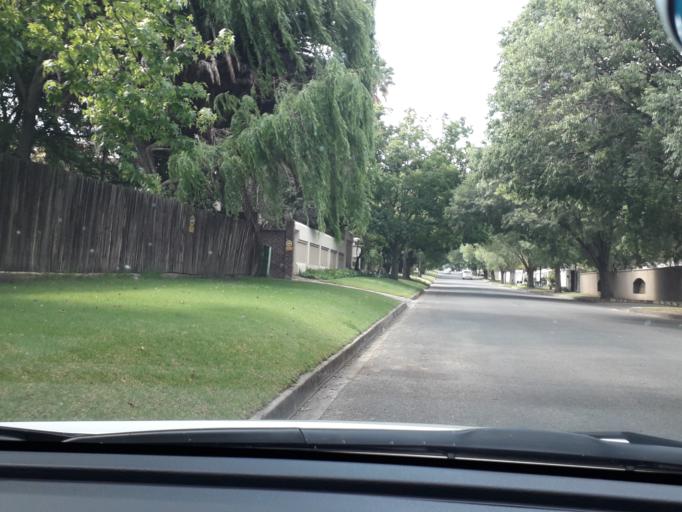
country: ZA
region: Gauteng
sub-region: City of Johannesburg Metropolitan Municipality
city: Johannesburg
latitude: -26.1548
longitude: 28.0700
